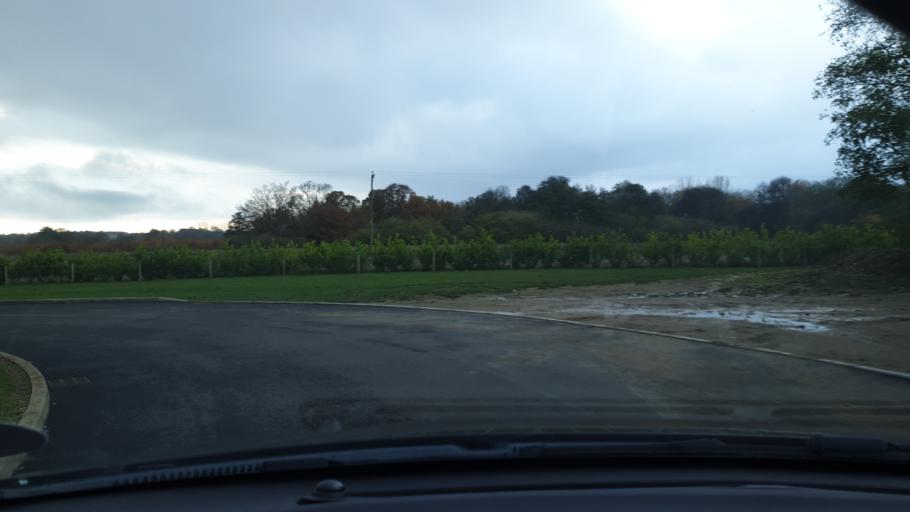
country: GB
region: England
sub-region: Essex
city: Alresford
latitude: 51.8731
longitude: 1.0101
